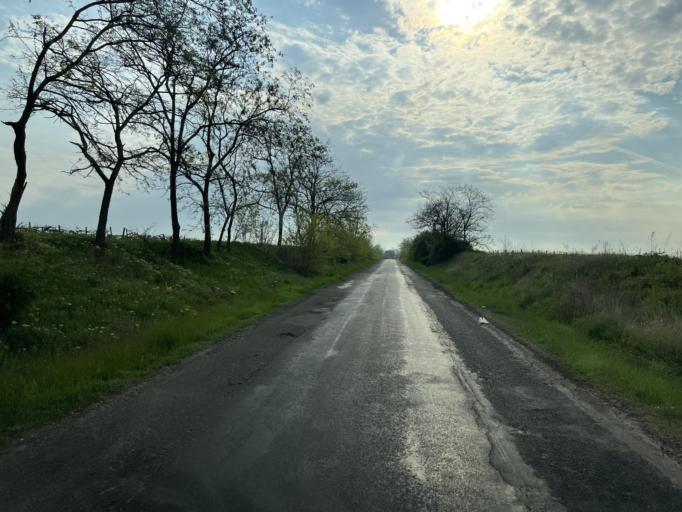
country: HU
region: Pest
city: Cegledbercel
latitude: 47.2173
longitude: 19.6954
